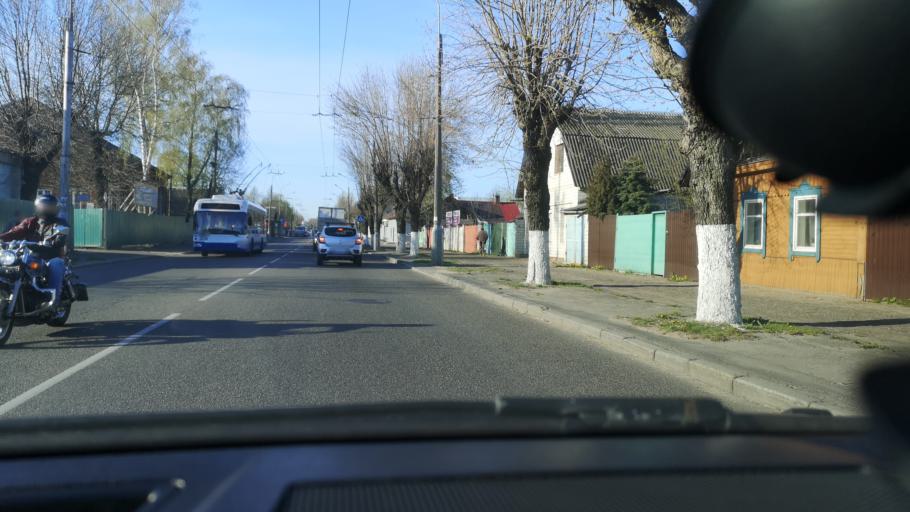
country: BY
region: Gomel
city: Gomel
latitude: 52.4344
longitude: 30.9763
